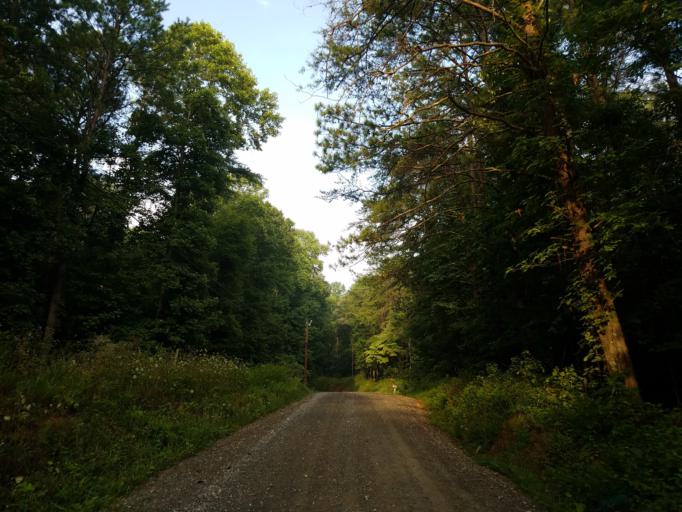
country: US
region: Georgia
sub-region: Pickens County
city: Jasper
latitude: 34.5484
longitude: -84.4410
